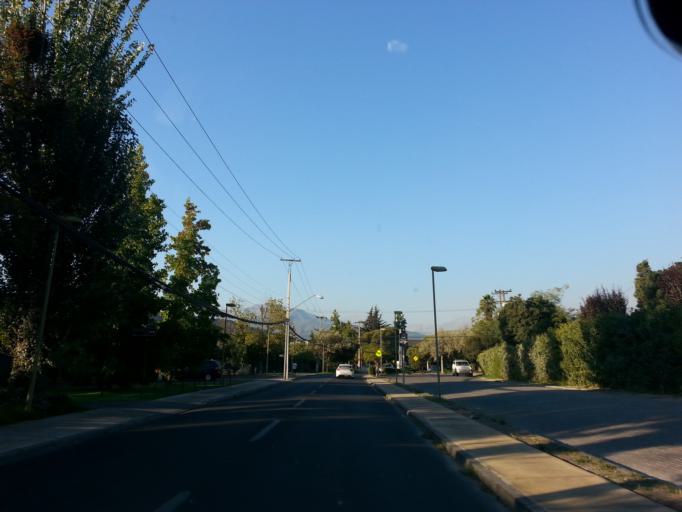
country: CL
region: Santiago Metropolitan
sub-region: Provincia de Santiago
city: Villa Presidente Frei, Nunoa, Santiago, Chile
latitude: -33.3915
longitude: -70.5377
